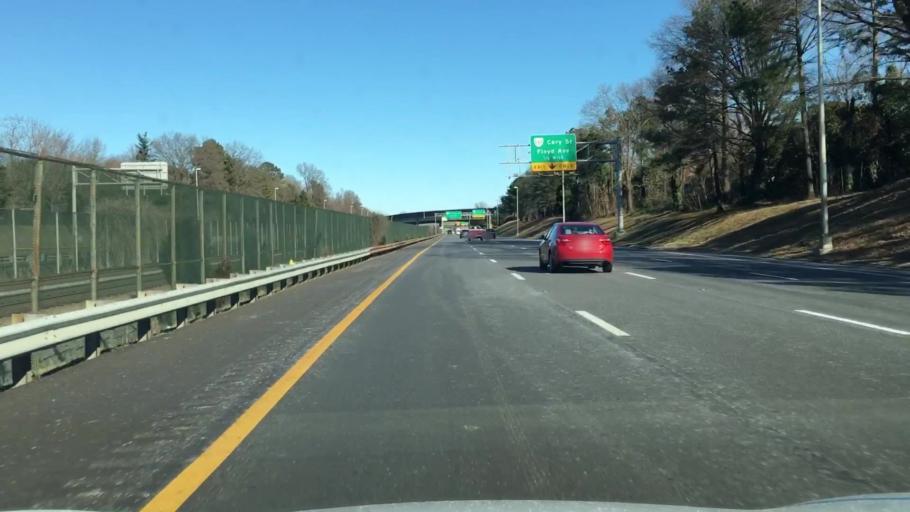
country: US
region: Virginia
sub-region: City of Richmond
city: Richmond
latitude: 37.5494
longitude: -77.4911
